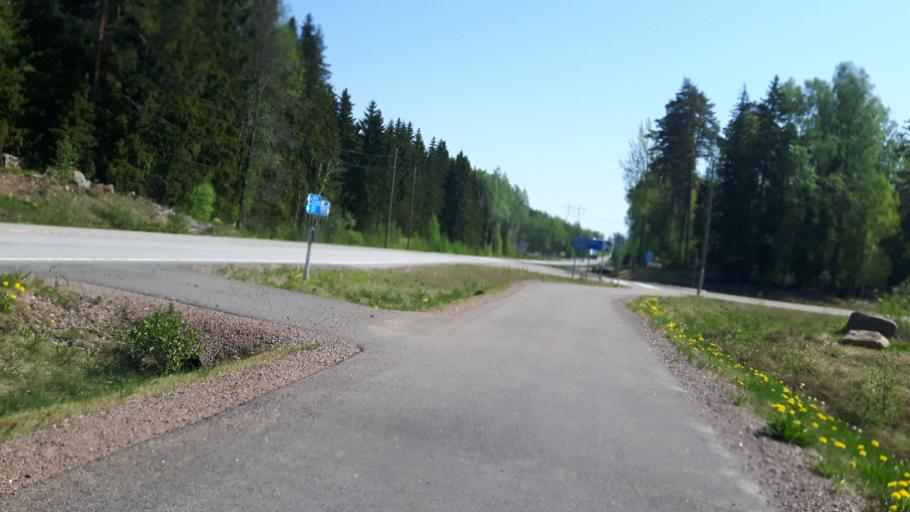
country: FI
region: Uusimaa
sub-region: Loviisa
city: Ruotsinpyhtaeae
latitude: 60.4948
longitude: 26.4436
